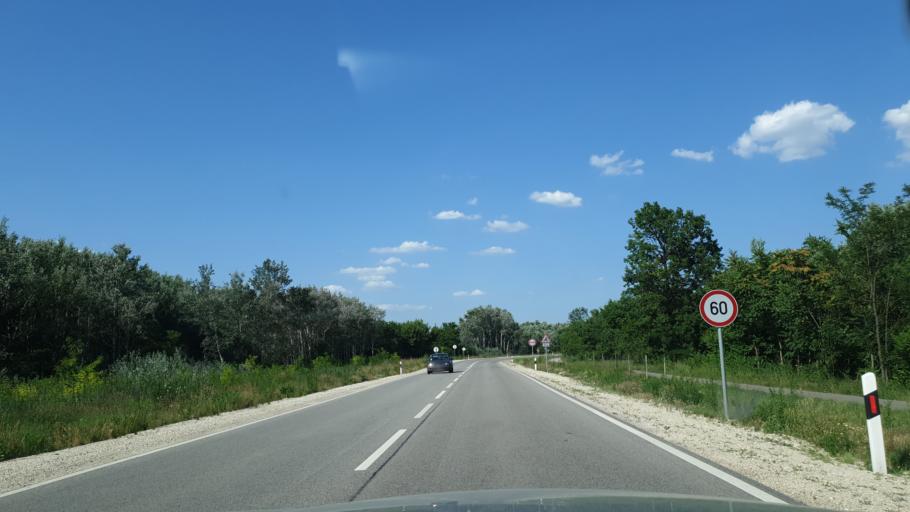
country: HU
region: Csongrad
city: Asotthalom
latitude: 46.2182
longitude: 19.8049
